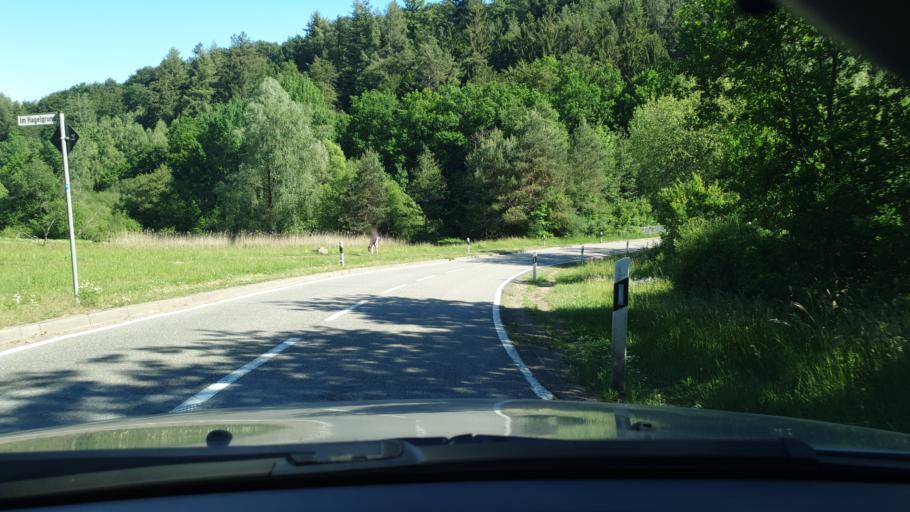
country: DE
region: Rheinland-Pfalz
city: Kaiserslautern
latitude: 49.4693
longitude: 7.7869
